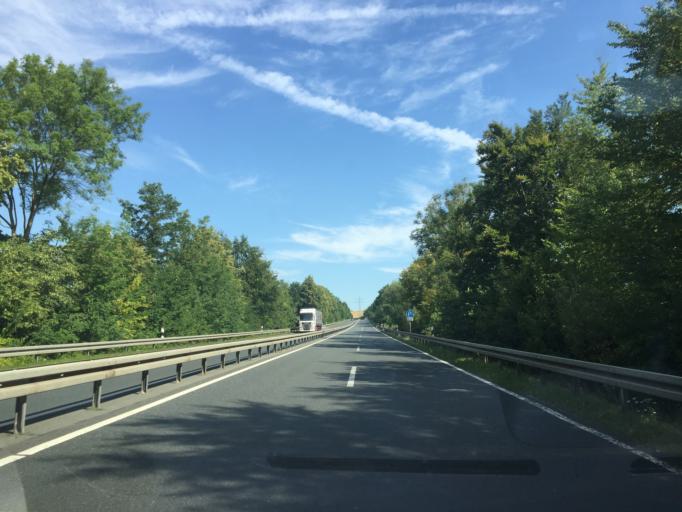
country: DE
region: Lower Saxony
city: Gittelde
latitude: 51.7917
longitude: 10.1970
